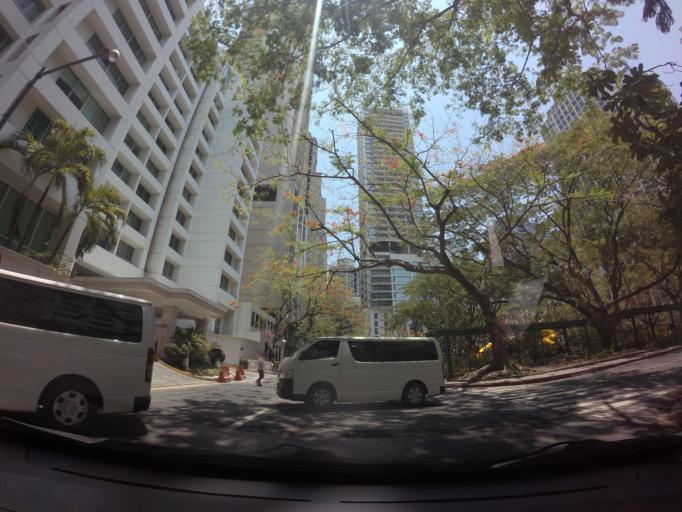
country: PH
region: Metro Manila
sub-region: Makati City
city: Makati City
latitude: 14.5606
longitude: 121.0223
